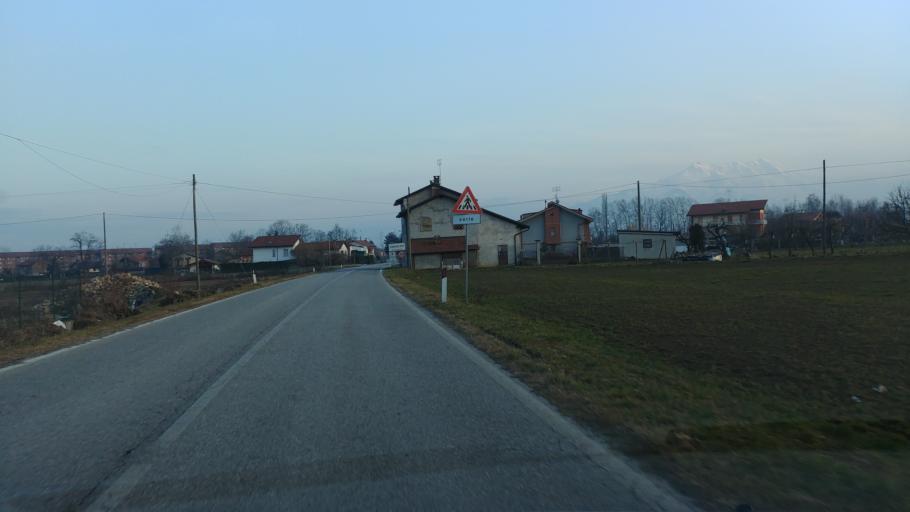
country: IT
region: Piedmont
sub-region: Provincia di Cuneo
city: Cuneo
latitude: 44.4050
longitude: 7.5236
